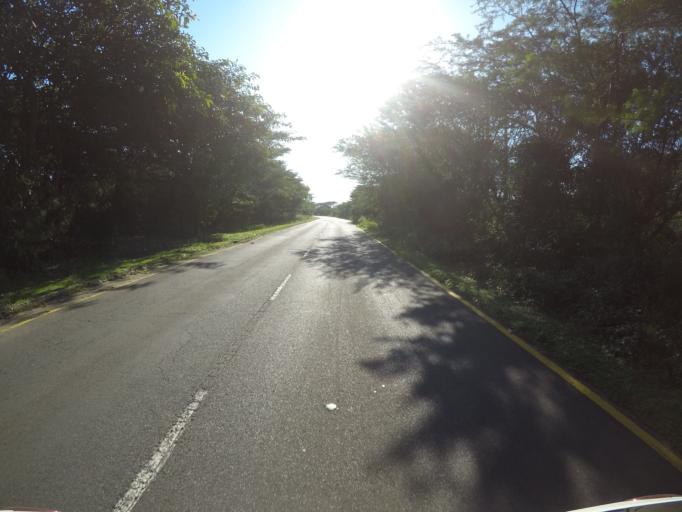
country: ZA
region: KwaZulu-Natal
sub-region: uThungulu District Municipality
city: Richards Bay
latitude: -28.7855
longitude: 32.0785
